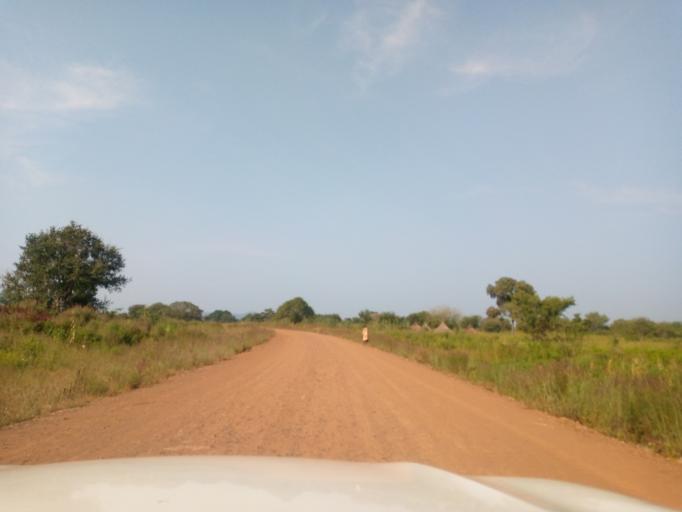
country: ET
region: Oromiya
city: Mendi
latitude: 10.1440
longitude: 34.9516
